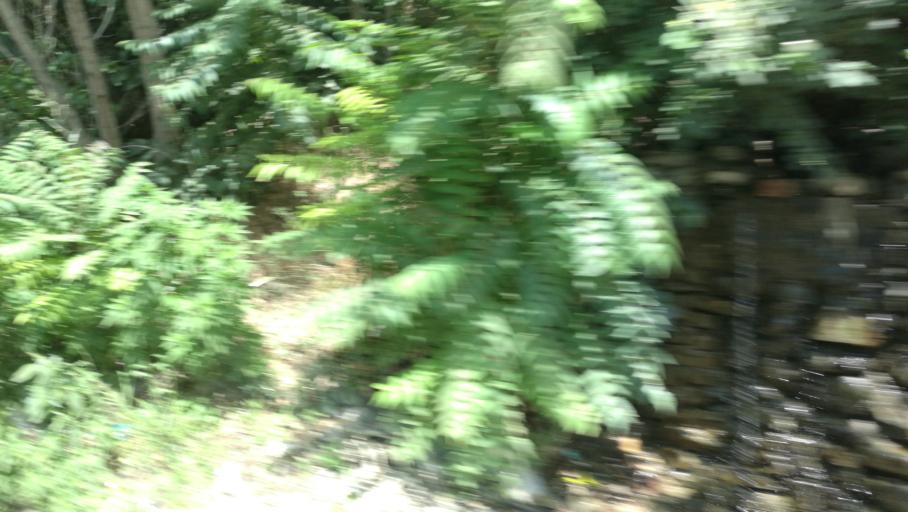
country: IR
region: Alborz
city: Karaj
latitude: 35.9382
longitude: 51.0697
